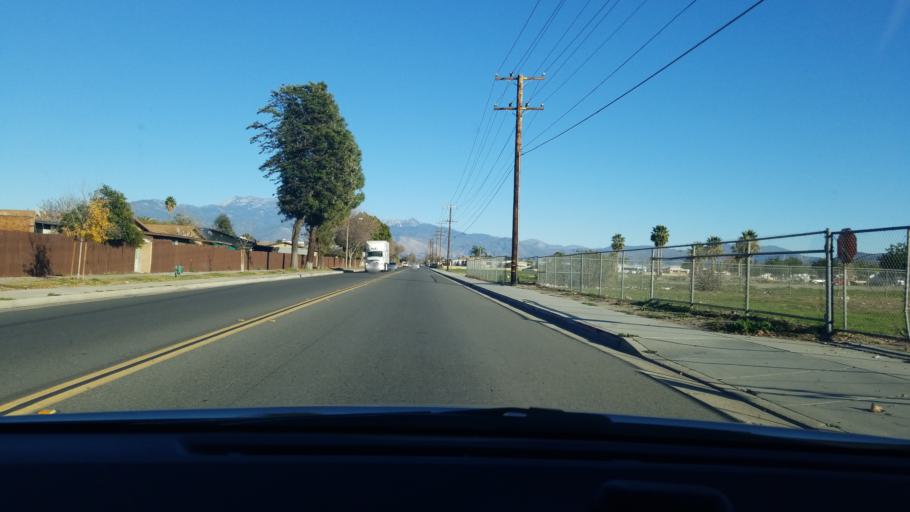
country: US
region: California
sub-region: Riverside County
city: Hemet
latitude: 33.7510
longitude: -116.9961
